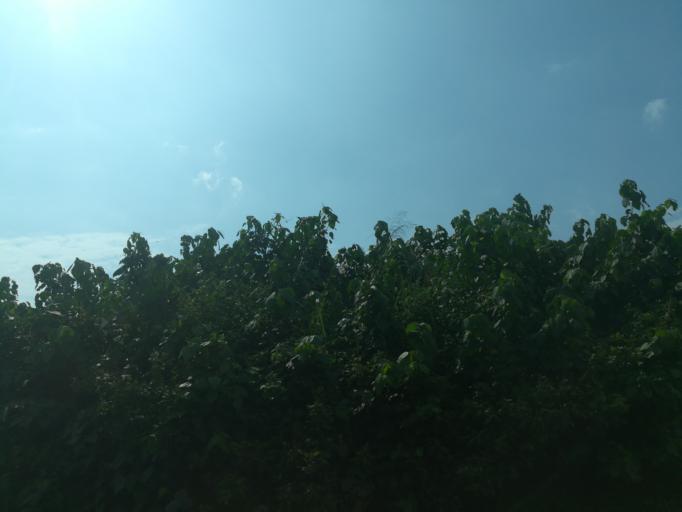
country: NG
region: Lagos
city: Ikorodu
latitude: 6.6317
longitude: 3.6671
